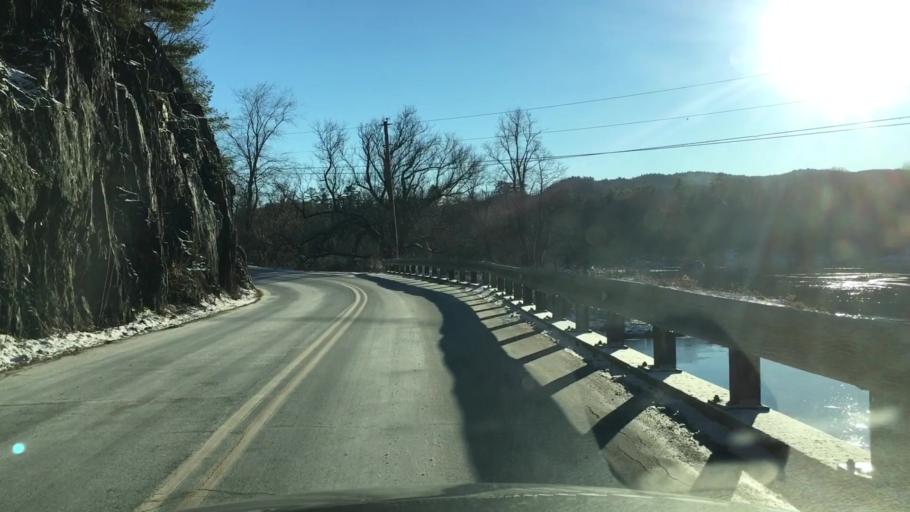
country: US
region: New Hampshire
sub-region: Grafton County
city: Woodsville
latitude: 44.1616
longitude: -72.0400
